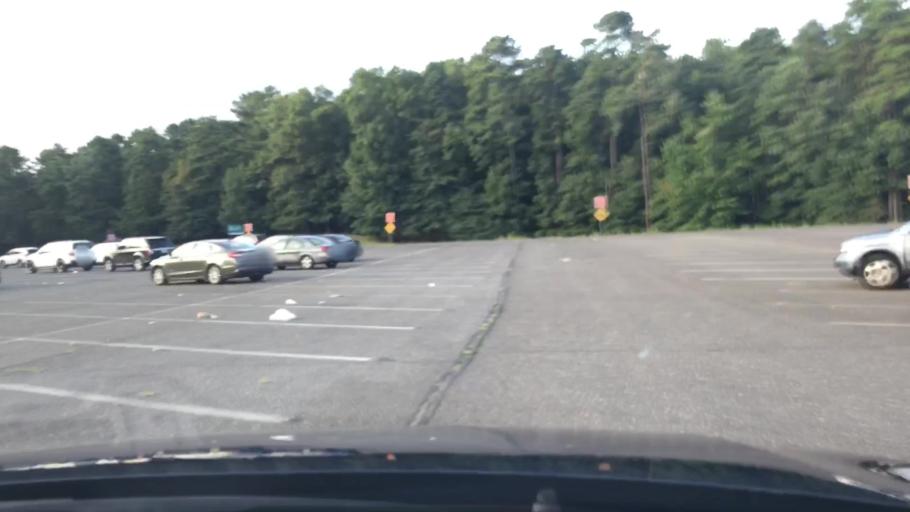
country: US
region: New Jersey
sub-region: Monmouth County
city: Shrewsbury
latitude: 40.1476
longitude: -74.4353
